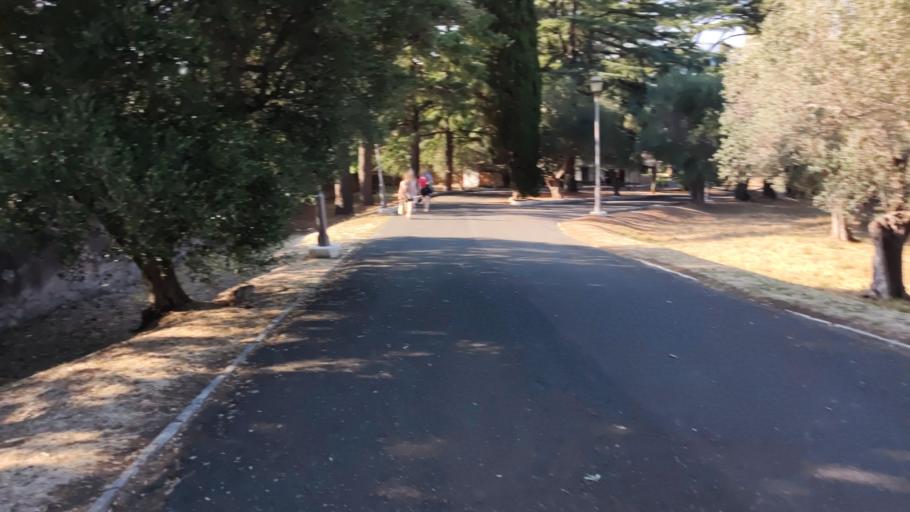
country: IT
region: Latium
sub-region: Citta metropolitana di Roma Capitale
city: Villa Adriana
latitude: 41.9450
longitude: 12.7721
